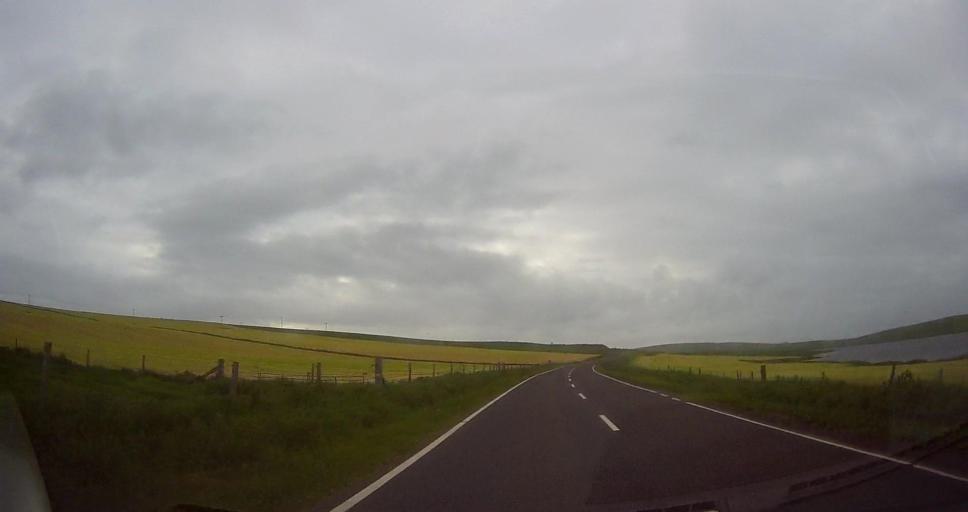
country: GB
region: Scotland
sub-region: Orkney Islands
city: Stromness
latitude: 58.9834
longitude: -3.2610
